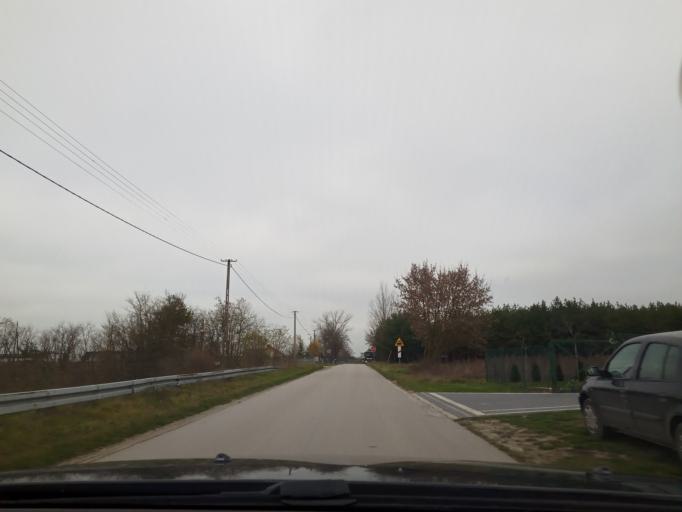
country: PL
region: Swietokrzyskie
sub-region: Powiat jedrzejowski
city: Imielno
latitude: 50.5922
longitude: 20.4790
